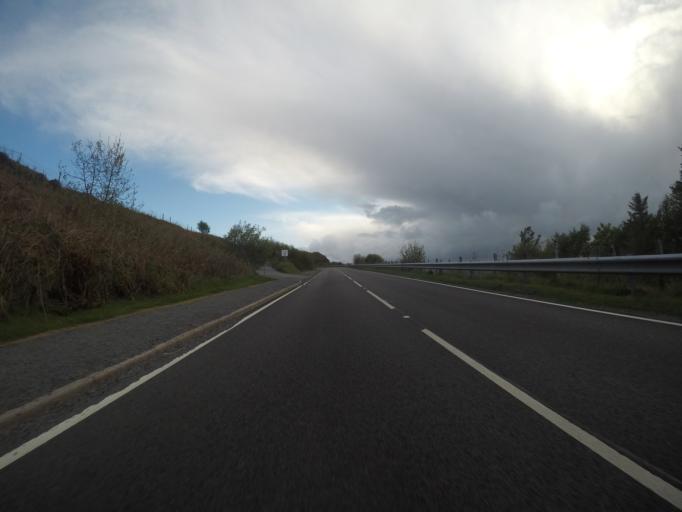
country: GB
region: Scotland
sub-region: Highland
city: Portree
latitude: 57.5824
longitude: -6.3588
